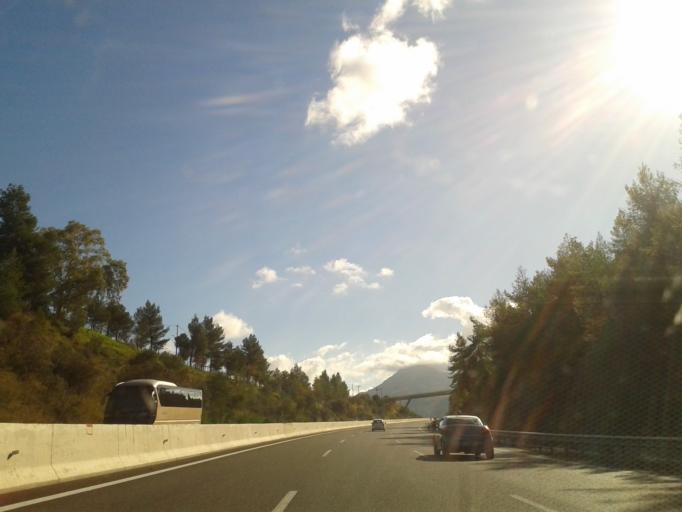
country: GR
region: West Greece
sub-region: Nomos Achaias
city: Aigio
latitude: 38.2529
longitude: 22.0693
